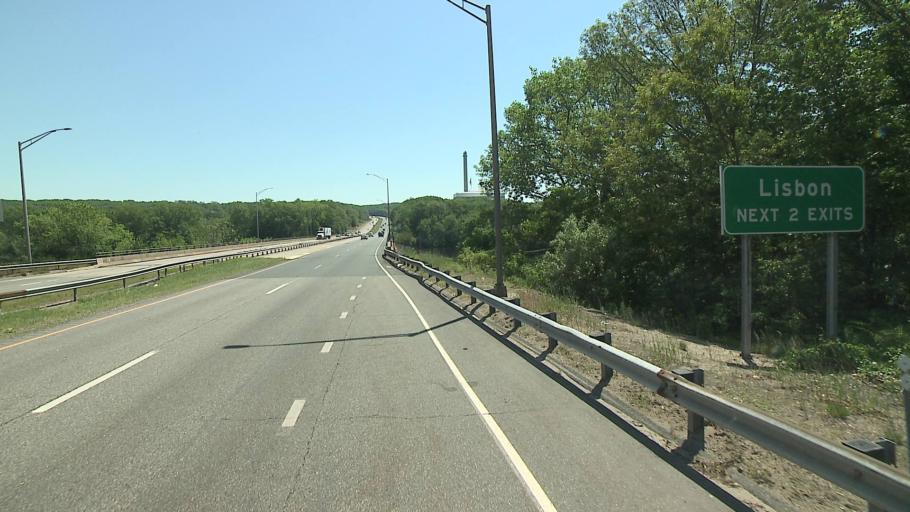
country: US
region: Connecticut
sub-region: New London County
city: Lisbon
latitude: 41.5851
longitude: -72.0480
